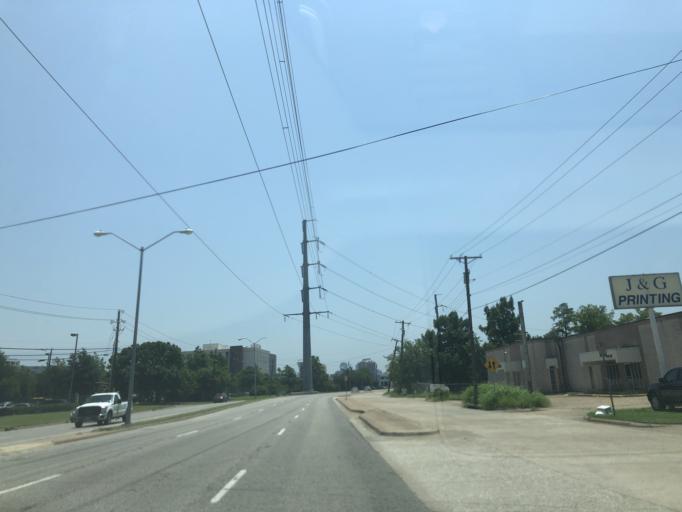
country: US
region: Texas
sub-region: Dallas County
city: Dallas
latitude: 32.8084
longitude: -96.8489
